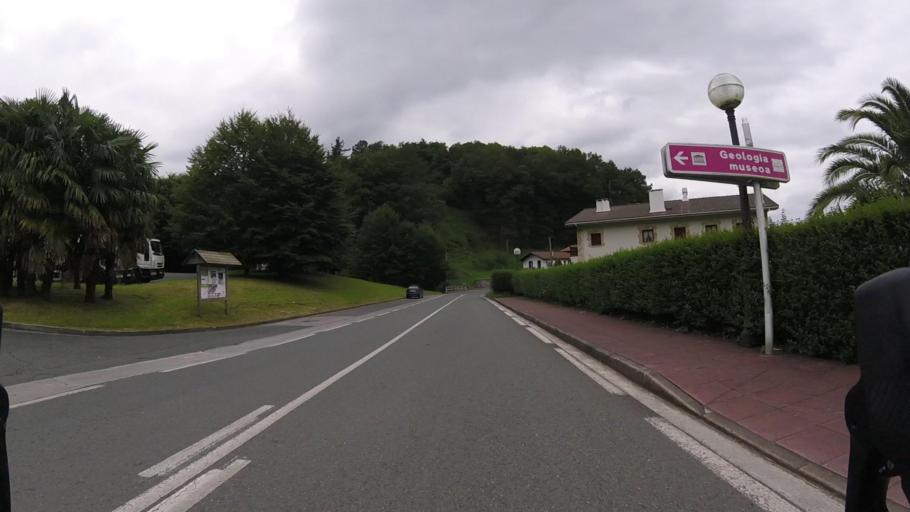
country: ES
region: Basque Country
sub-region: Provincia de Guipuzcoa
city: Irun
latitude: 43.2866
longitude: -1.8335
